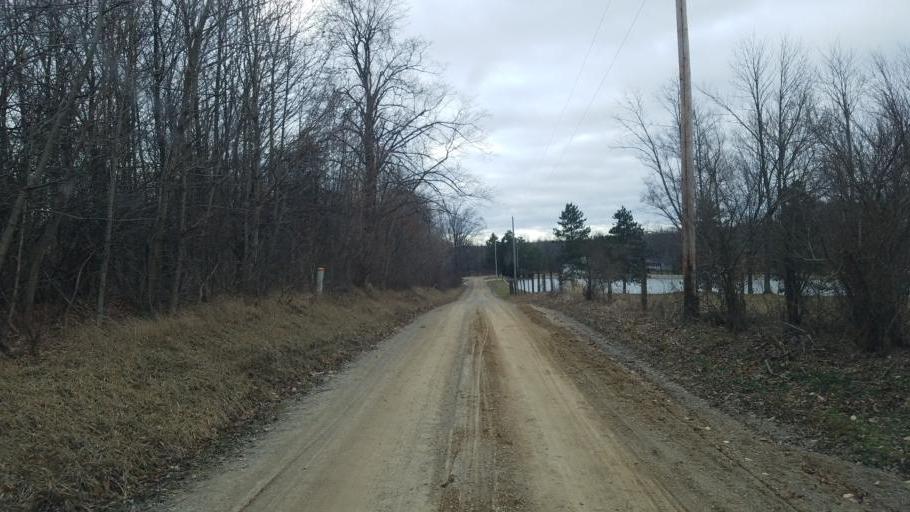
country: US
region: Ohio
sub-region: Richland County
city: Lexington
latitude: 40.5744
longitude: -82.6764
